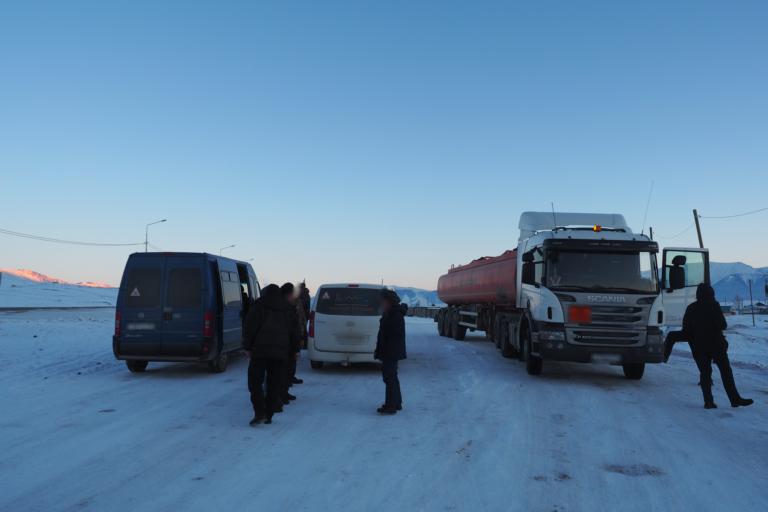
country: RU
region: Altay
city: Aktash
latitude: 50.2359
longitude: 87.9256
